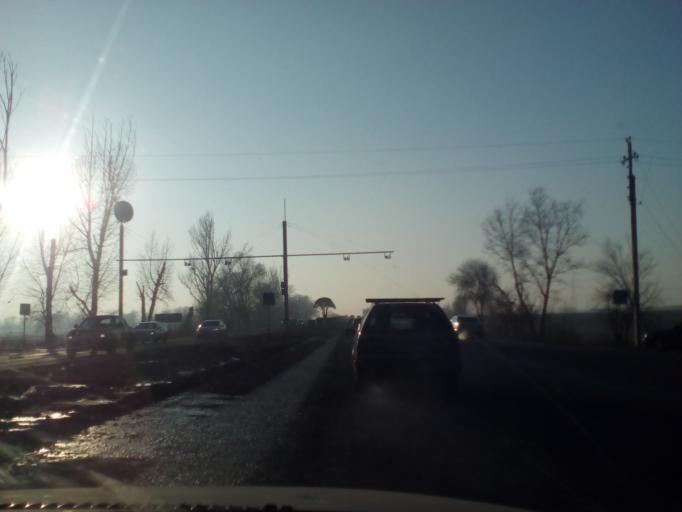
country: KZ
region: Almaty Oblysy
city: Burunday
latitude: 43.2237
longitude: 76.6016
